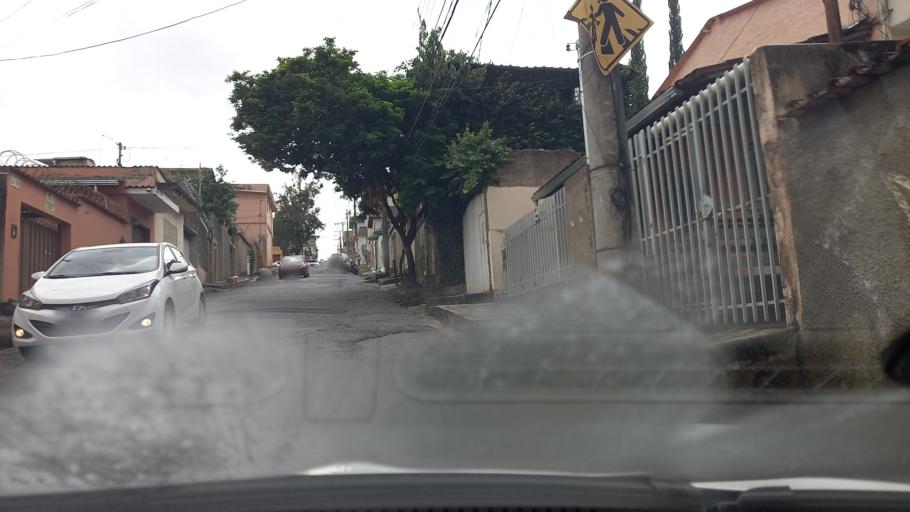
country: BR
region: Minas Gerais
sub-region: Contagem
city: Contagem
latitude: -19.9104
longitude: -44.0014
